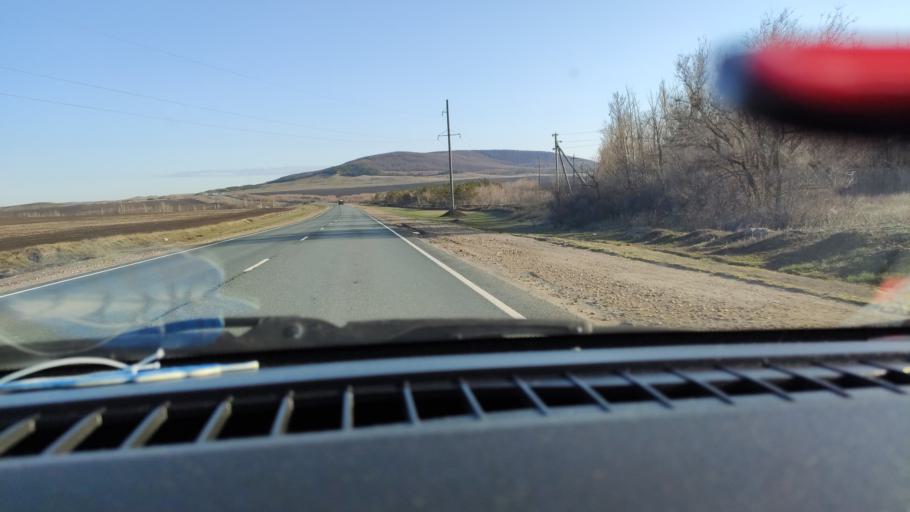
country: RU
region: Saratov
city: Alekseyevka
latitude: 52.2769
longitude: 47.9313
